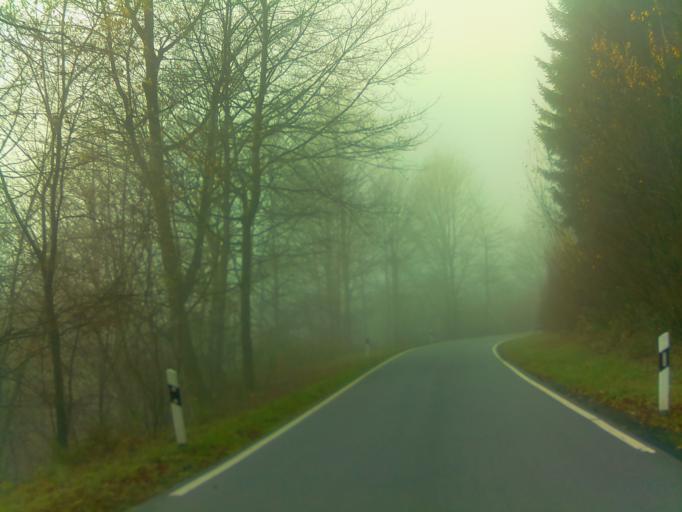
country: DE
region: Baden-Wuerttemberg
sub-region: Karlsruhe Region
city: Heddesbach
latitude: 49.4971
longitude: 8.8376
